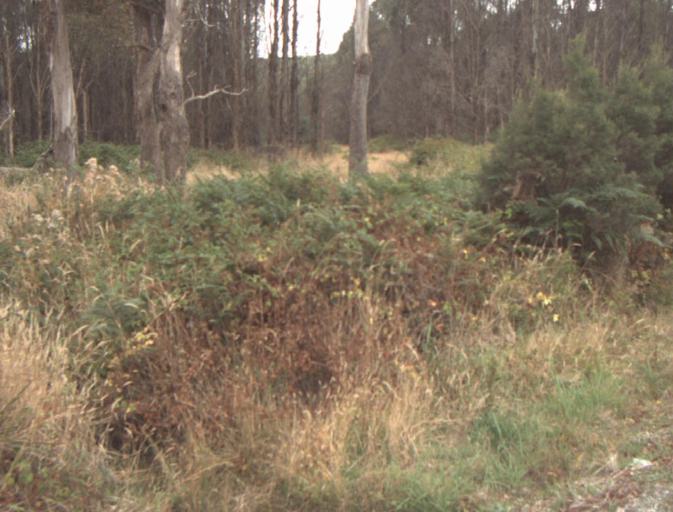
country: AU
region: Tasmania
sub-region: Launceston
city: Mayfield
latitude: -41.2379
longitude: 147.1803
